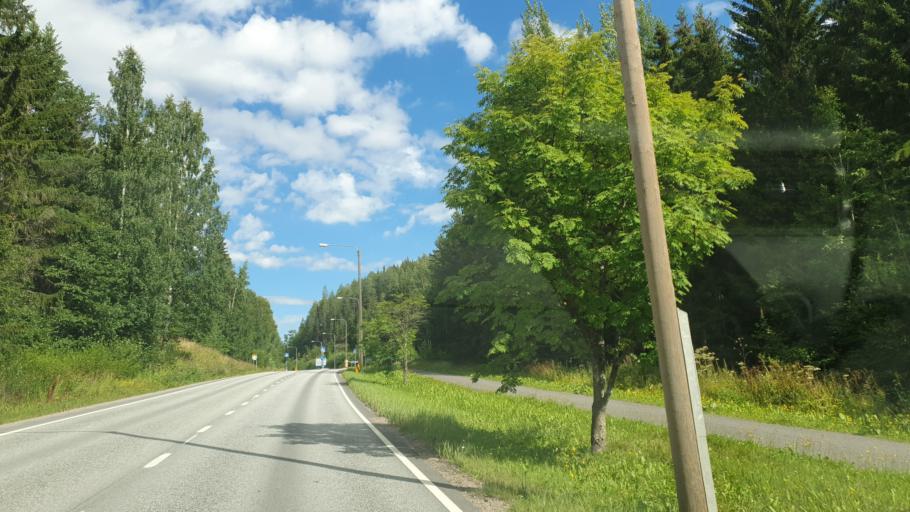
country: FI
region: Central Finland
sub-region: Jyvaeskylae
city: Muurame
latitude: 62.1391
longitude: 25.6925
